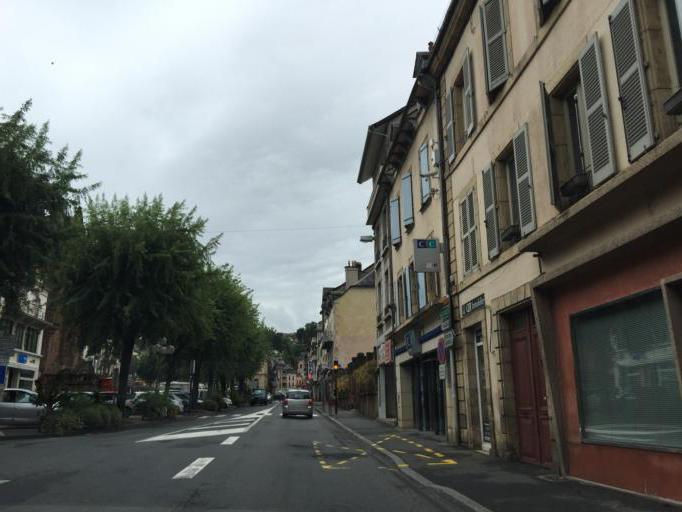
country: FR
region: Midi-Pyrenees
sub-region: Departement de l'Aveyron
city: Espalion
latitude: 44.5220
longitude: 2.7623
